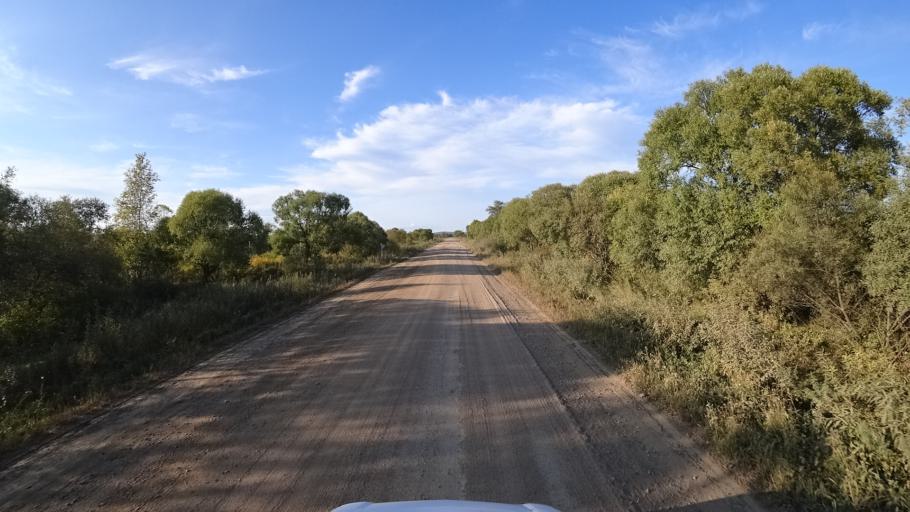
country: RU
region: Amur
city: Arkhara
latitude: 49.3561
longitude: 130.1375
